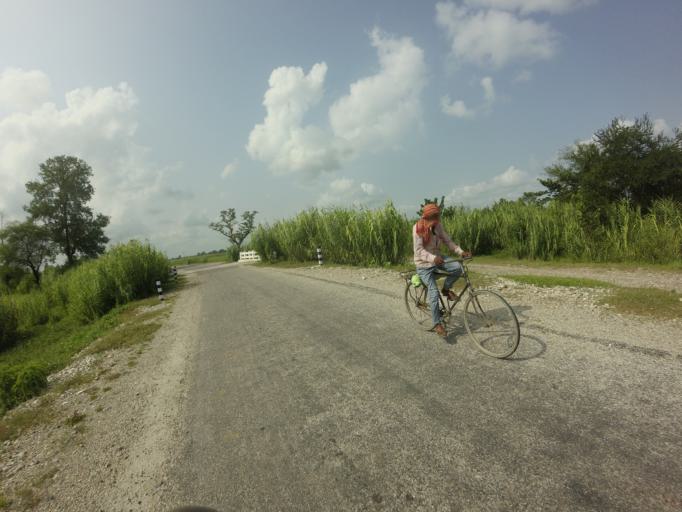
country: NP
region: Far Western
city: Tikapur
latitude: 28.4697
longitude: 81.0741
